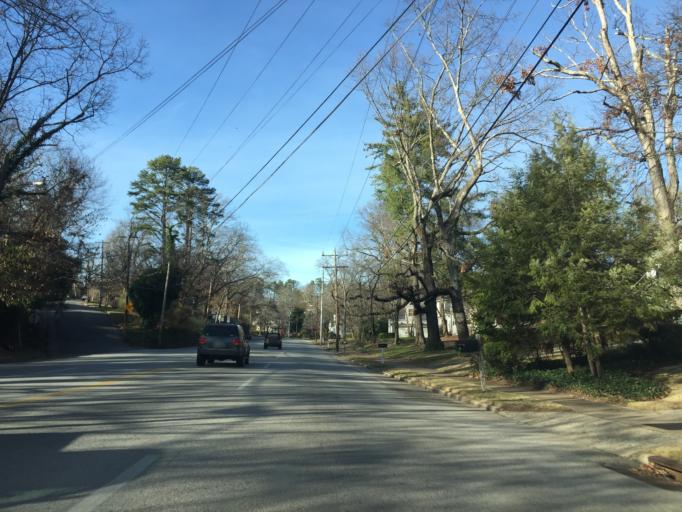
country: US
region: Tennessee
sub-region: Hamilton County
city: Chattanooga
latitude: 35.0755
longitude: -85.2882
